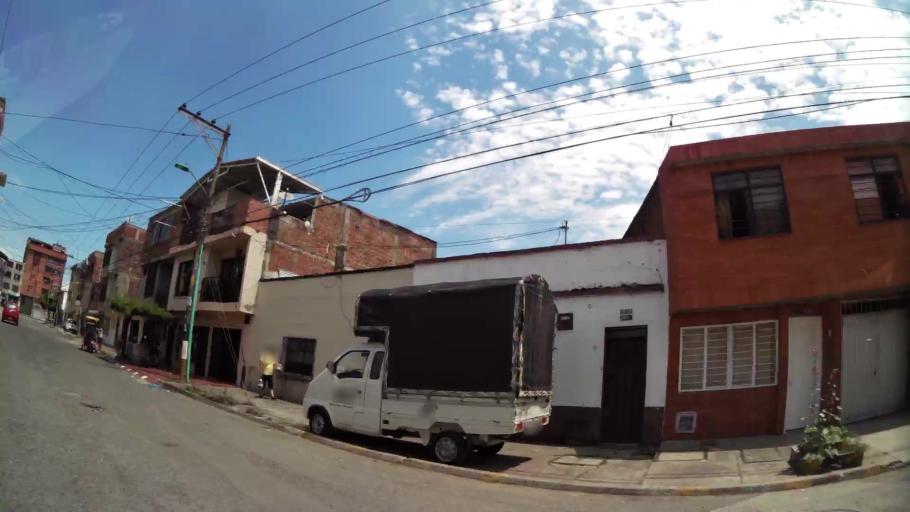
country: CO
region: Valle del Cauca
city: Cali
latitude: 3.4390
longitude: -76.5159
